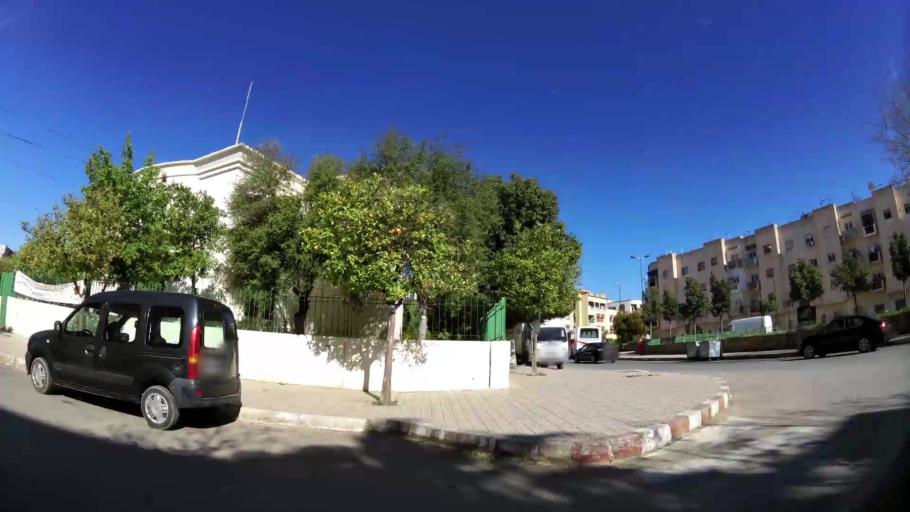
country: MA
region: Meknes-Tafilalet
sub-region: Meknes
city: Meknes
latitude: 33.8919
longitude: -5.5012
